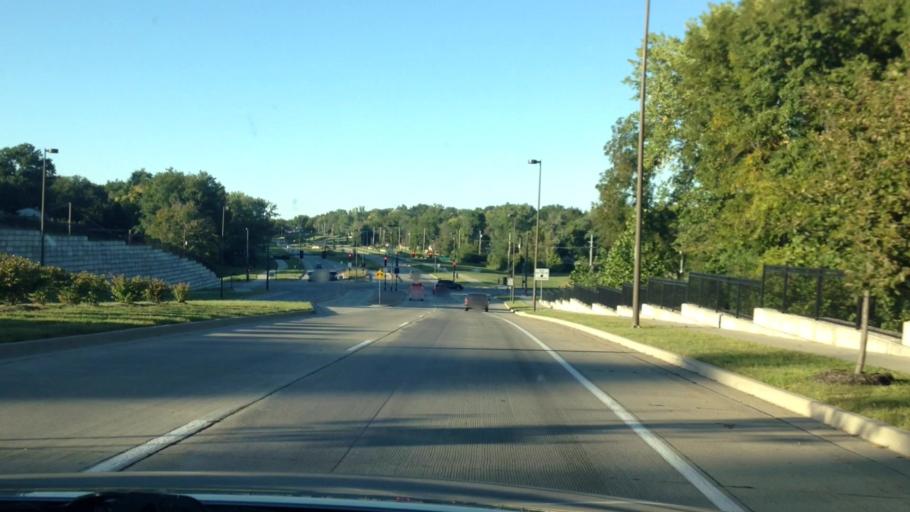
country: US
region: Missouri
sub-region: Clay County
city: North Kansas City
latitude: 39.1608
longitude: -94.5328
